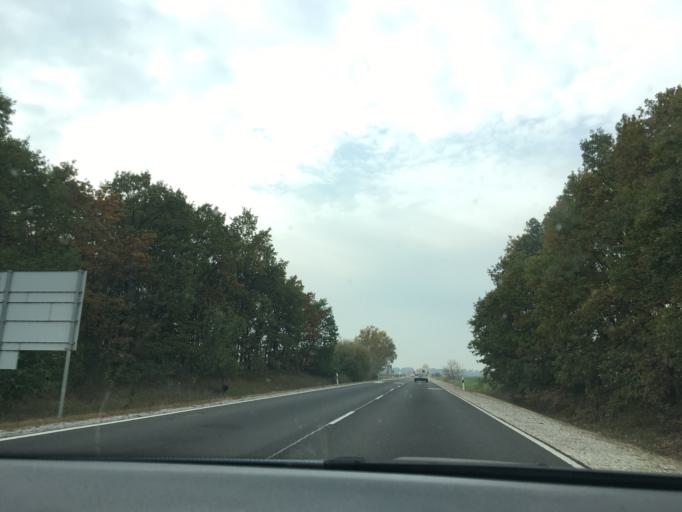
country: HU
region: Jasz-Nagykun-Szolnok
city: Toszeg
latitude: 47.1467
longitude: 20.1541
